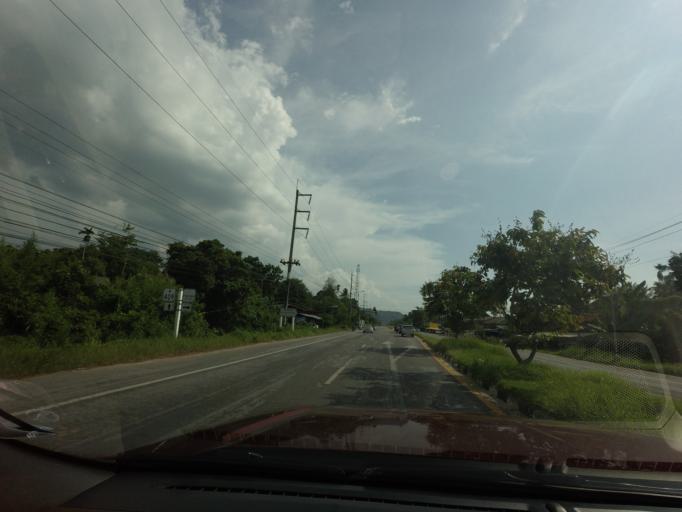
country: TH
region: Yala
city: Yala
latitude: 6.5476
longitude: 101.2534
